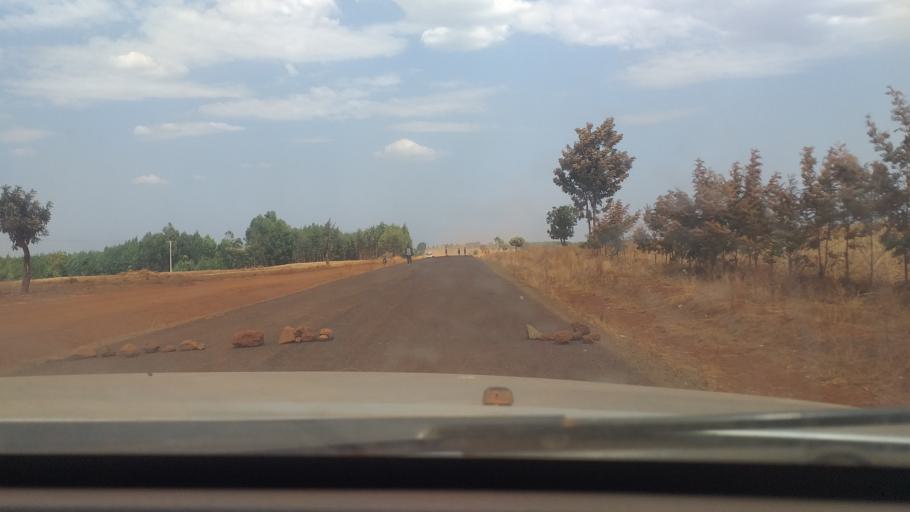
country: ET
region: Binshangul Gumuz
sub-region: Asosa
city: Asosa
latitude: 10.0780
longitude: 34.6395
